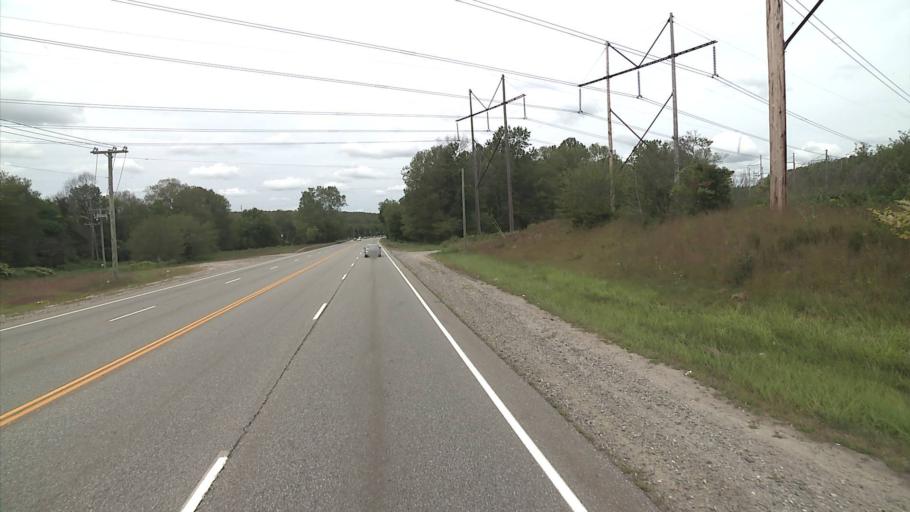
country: US
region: Connecticut
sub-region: New London County
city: Central Waterford
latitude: 41.3820
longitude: -72.1538
